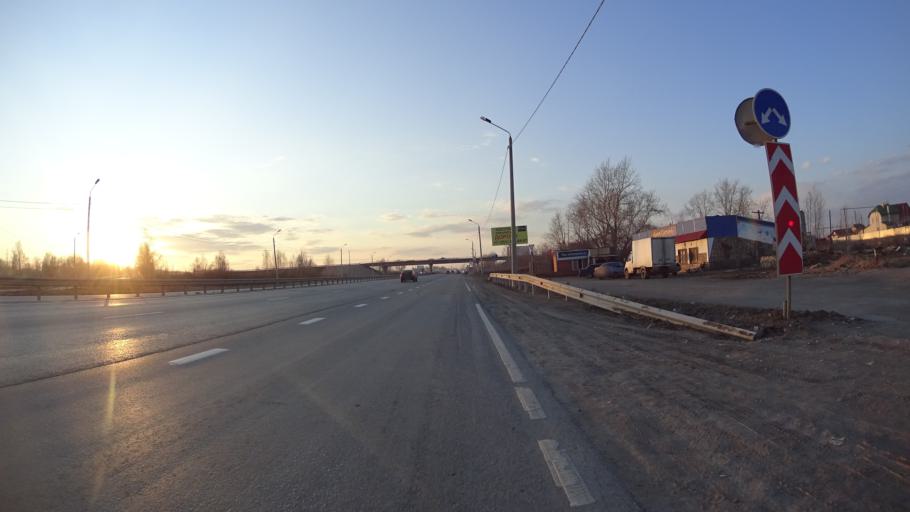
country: RU
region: Chelyabinsk
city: Novosineglazovskiy
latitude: 55.0603
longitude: 61.4023
